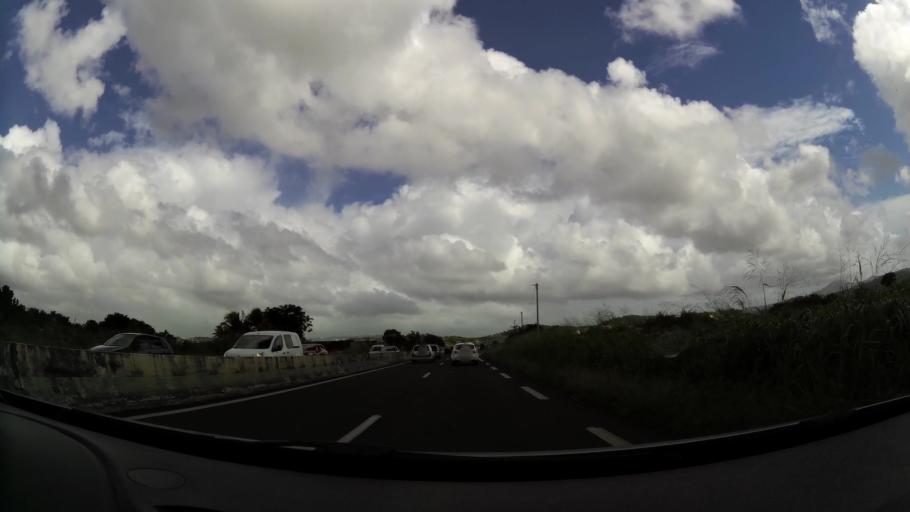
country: MQ
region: Martinique
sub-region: Martinique
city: Ducos
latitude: 14.5414
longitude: -60.9773
